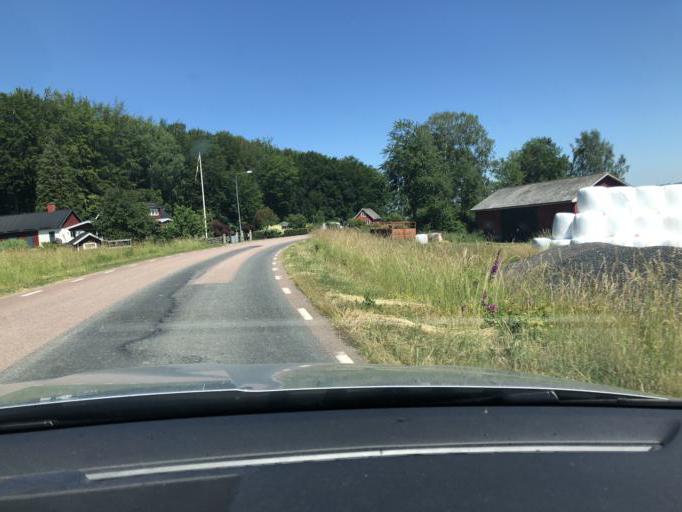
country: SE
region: Blekinge
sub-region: Olofstroms Kommun
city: Jamshog
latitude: 56.1674
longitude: 14.5994
